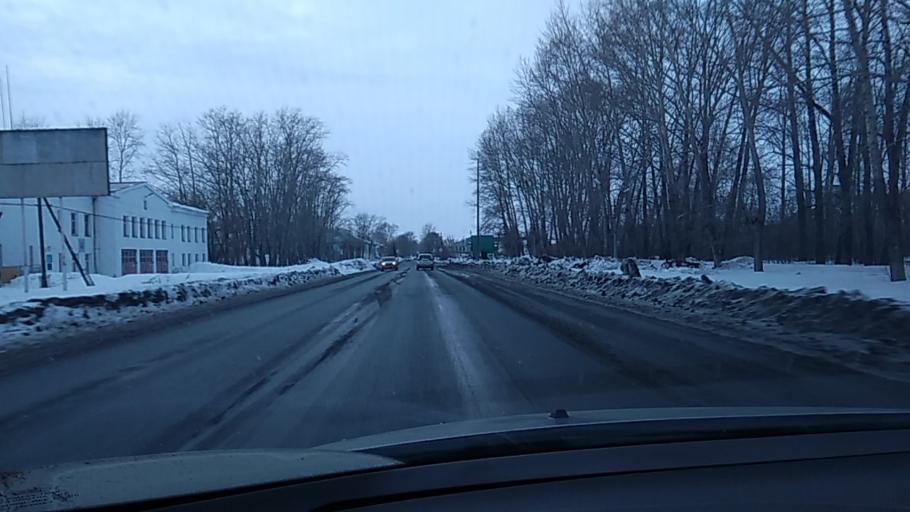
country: RU
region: Sverdlovsk
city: Martyush
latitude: 56.4444
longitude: 61.8224
